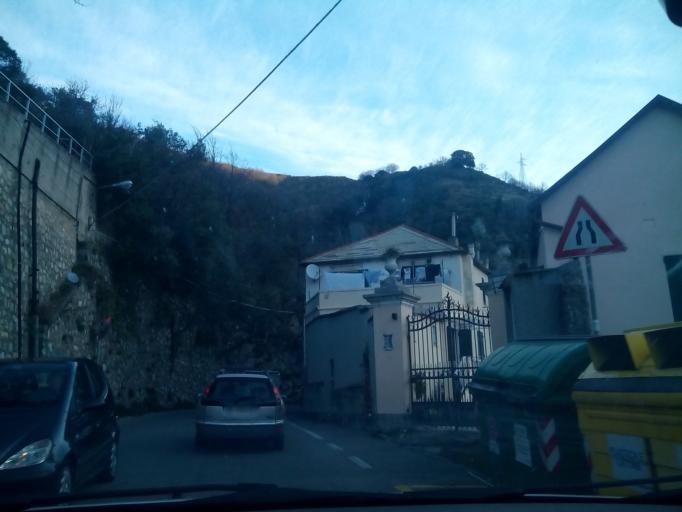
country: IT
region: Liguria
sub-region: Provincia di Genova
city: Piccarello
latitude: 44.4136
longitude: 8.9920
